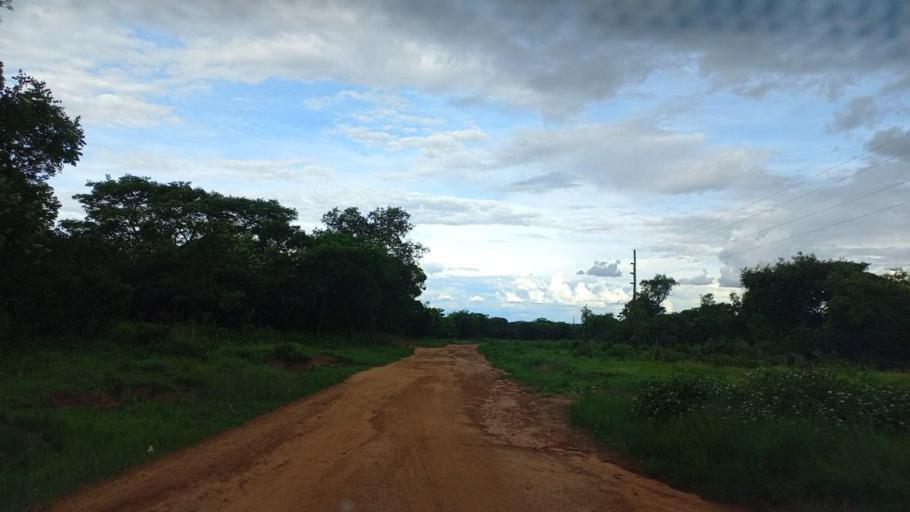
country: ZM
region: North-Western
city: Mwinilunga
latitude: -11.7742
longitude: 24.3920
